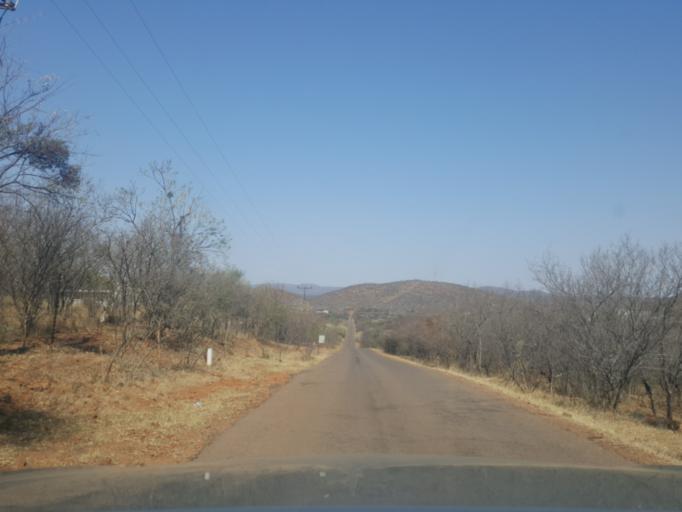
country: BW
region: Kweneng
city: Gabane
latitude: -24.7405
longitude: 25.8191
